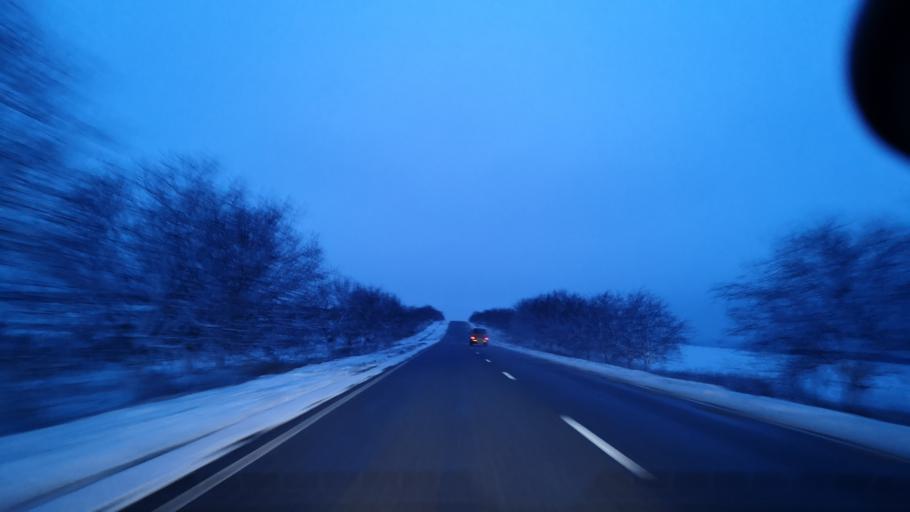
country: MD
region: Rezina
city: Saharna
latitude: 47.6213
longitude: 28.8333
